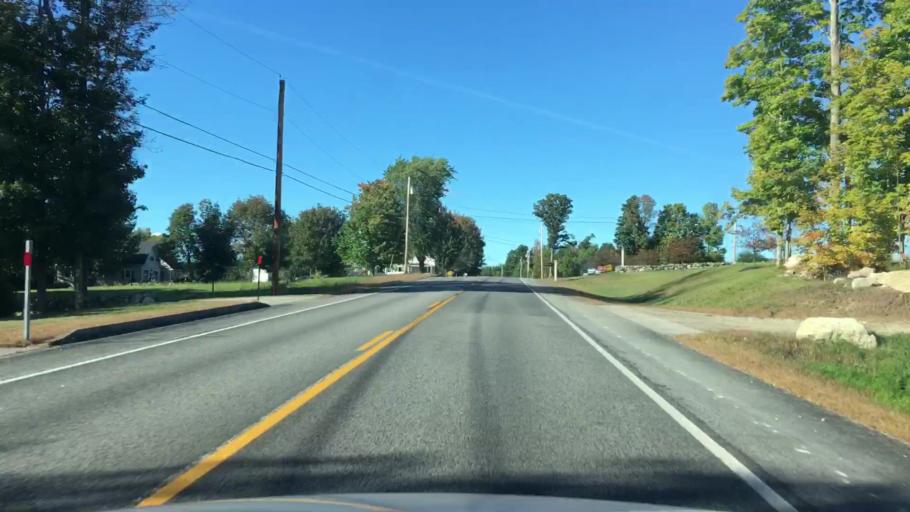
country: US
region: Maine
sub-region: Androscoggin County
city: Lisbon Falls
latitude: 44.0266
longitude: -70.0674
